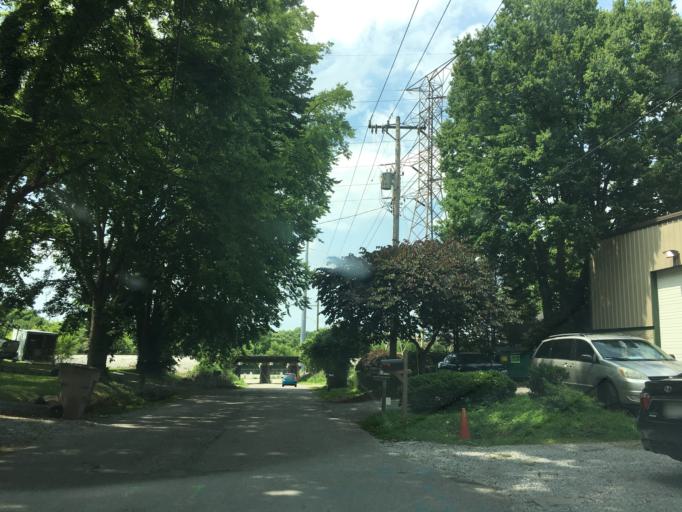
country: US
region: Tennessee
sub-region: Davidson County
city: Nashville
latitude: 36.1281
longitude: -86.7598
